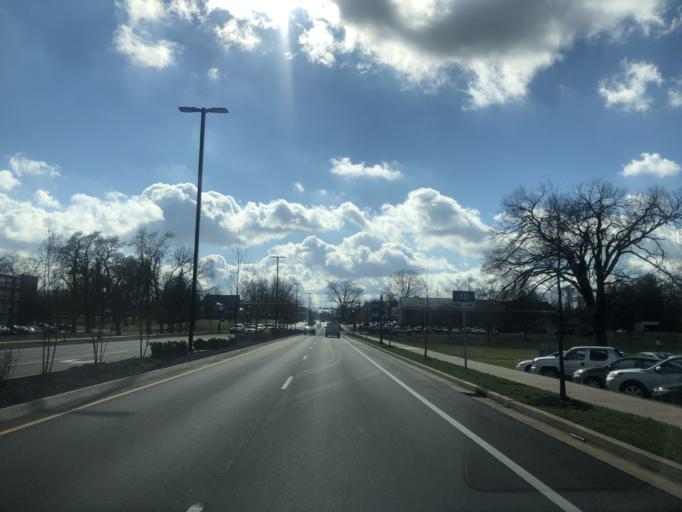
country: US
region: Tennessee
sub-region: Rutherford County
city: Murfreesboro
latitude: 35.8478
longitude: -86.3716
